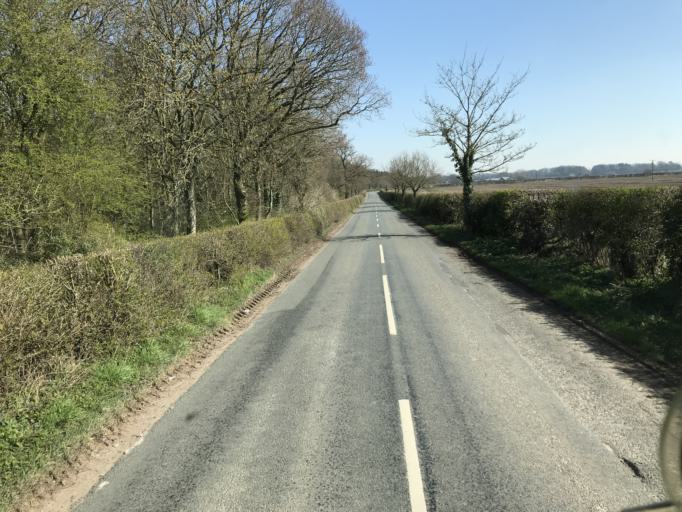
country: GB
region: England
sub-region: Cheshire West and Chester
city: Aldford
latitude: 53.1315
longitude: -2.8597
